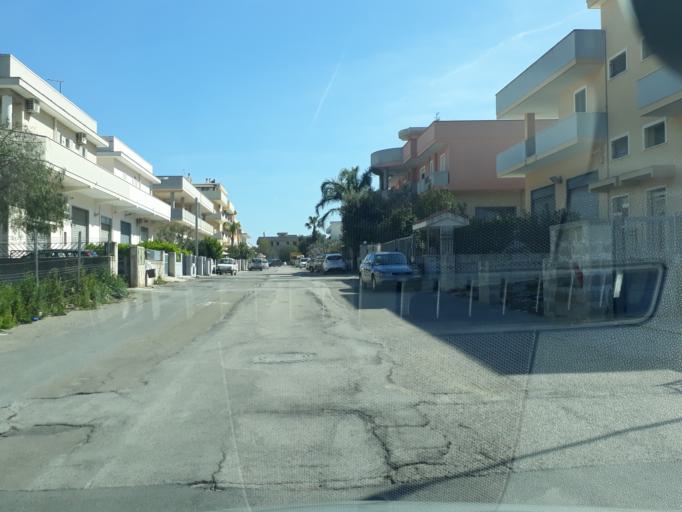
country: IT
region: Apulia
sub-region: Provincia di Brindisi
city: Fasano
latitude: 40.8473
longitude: 17.3503
